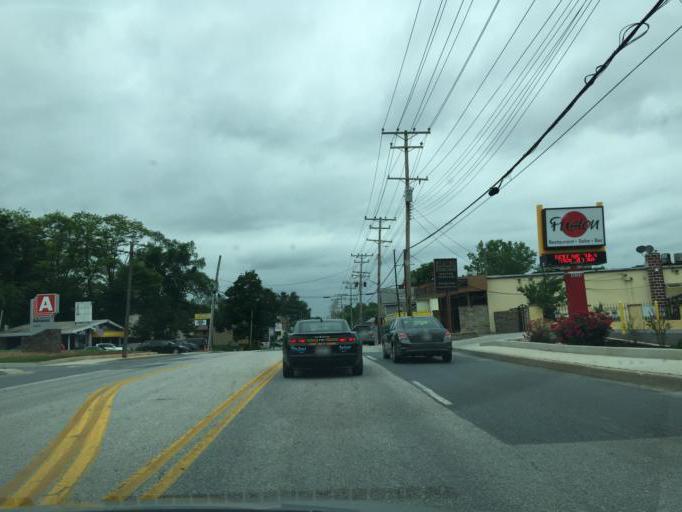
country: US
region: Maryland
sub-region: Baltimore County
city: Cockeysville
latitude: 39.4813
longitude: -76.6439
